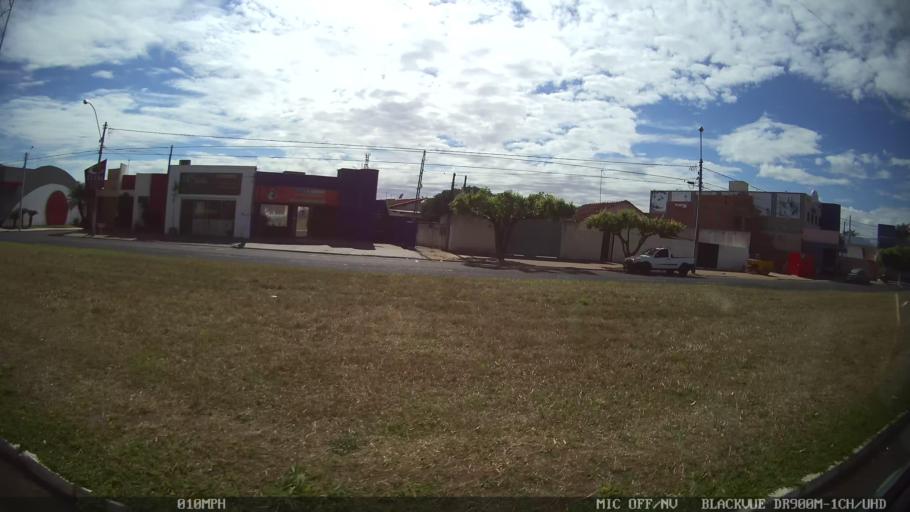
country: BR
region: Sao Paulo
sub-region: Bady Bassitt
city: Bady Bassitt
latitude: -20.8132
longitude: -49.5013
